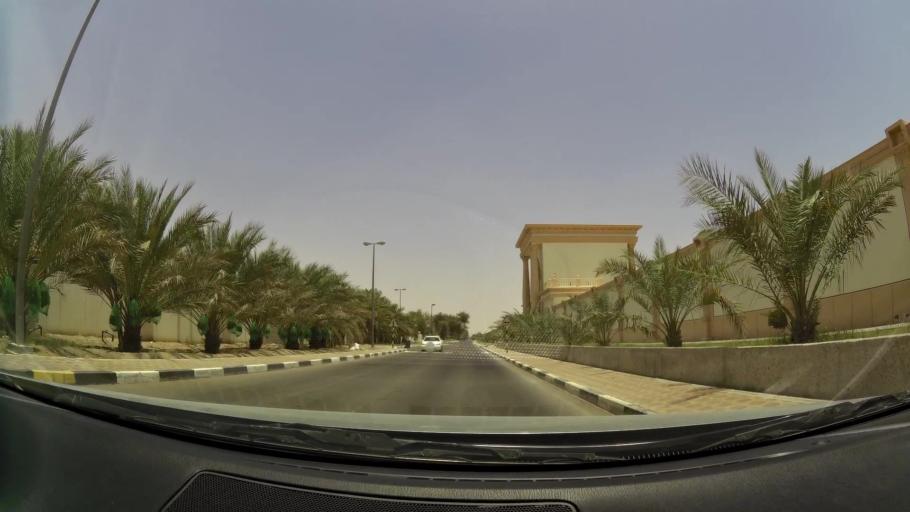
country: OM
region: Al Buraimi
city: Al Buraymi
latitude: 24.2785
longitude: 55.7369
